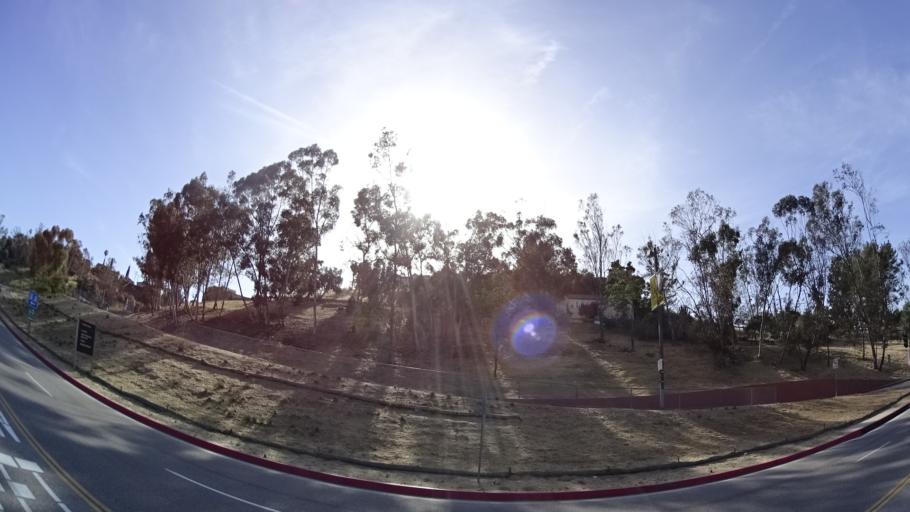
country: US
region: California
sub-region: Los Angeles County
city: Belvedere
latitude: 34.0702
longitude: -118.1691
